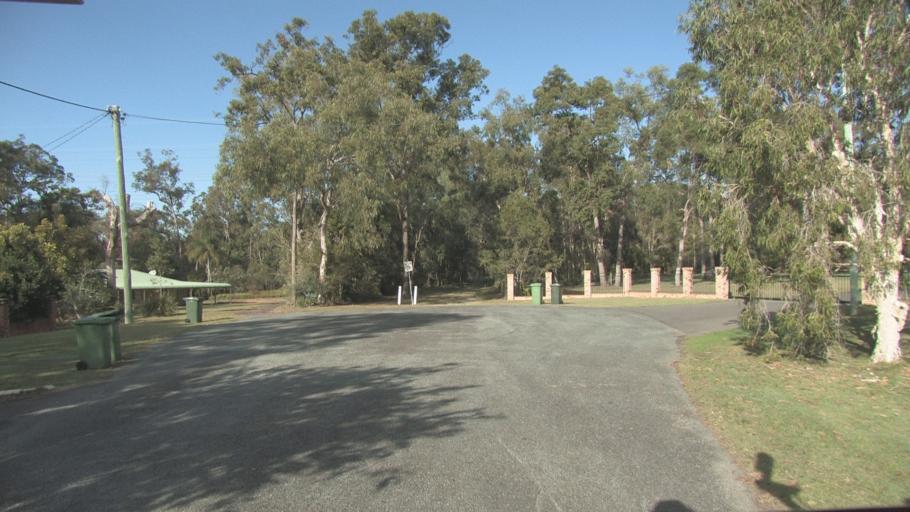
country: AU
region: Queensland
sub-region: Logan
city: Park Ridge South
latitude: -27.7342
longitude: 153.0350
